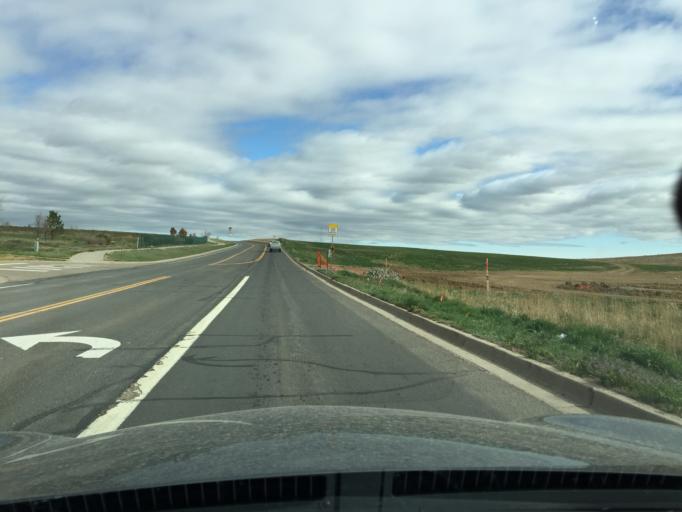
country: US
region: Colorado
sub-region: Boulder County
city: Erie
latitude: 40.0025
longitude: -105.0080
